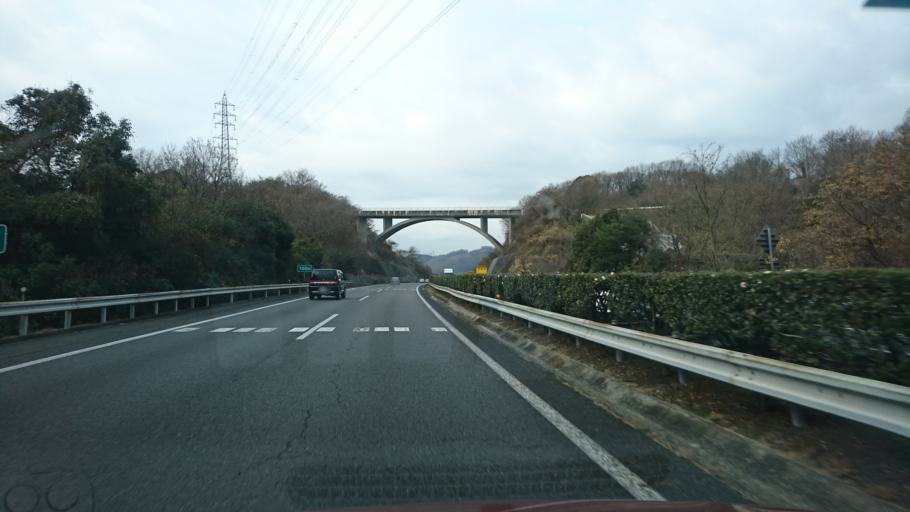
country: JP
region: Okayama
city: Kurashiki
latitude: 34.6044
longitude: 133.7216
